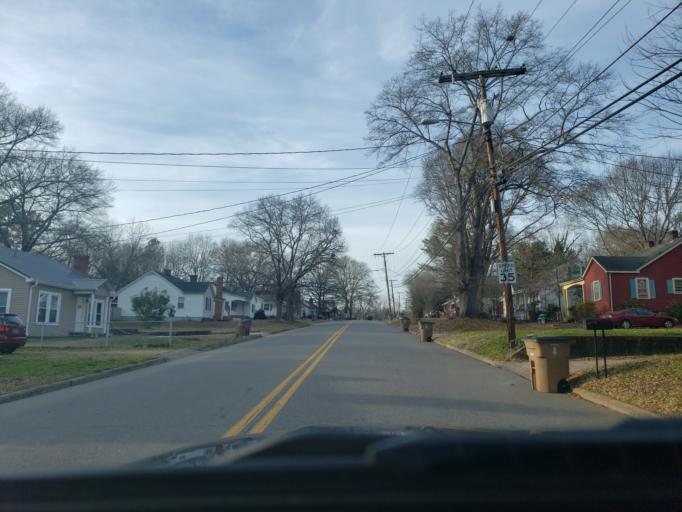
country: US
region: North Carolina
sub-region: Cleveland County
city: Shelby
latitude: 35.2840
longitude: -81.5266
